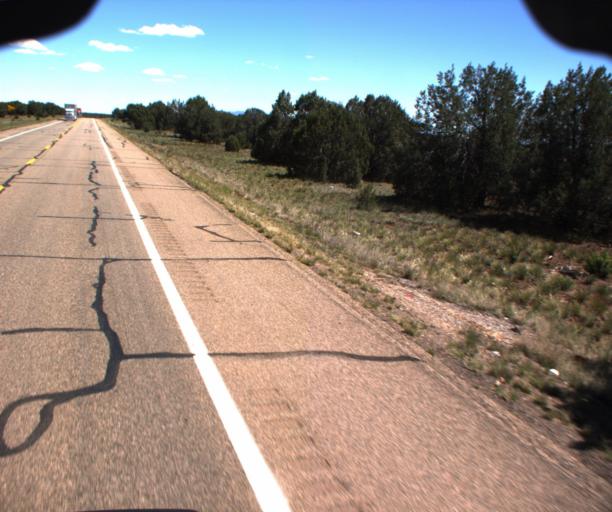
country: US
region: Arizona
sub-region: Yavapai County
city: Paulden
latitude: 35.0913
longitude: -112.4154
